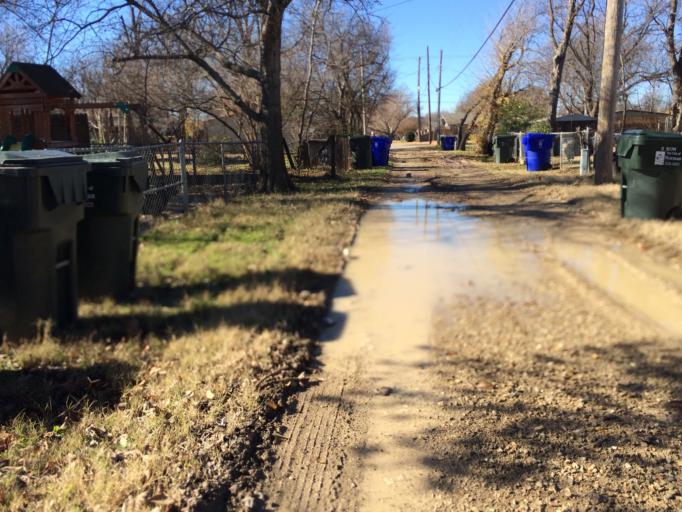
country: US
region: Oklahoma
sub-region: Cleveland County
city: Norman
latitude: 35.2226
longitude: -97.4581
